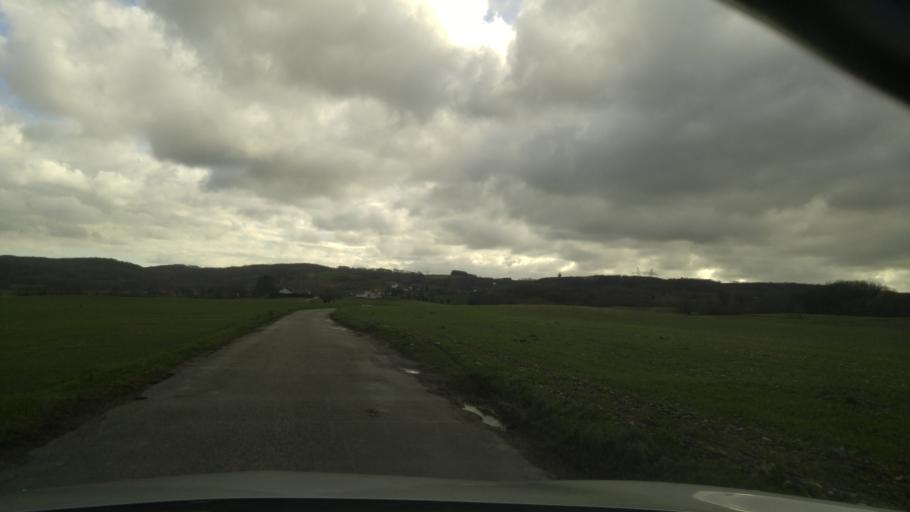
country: FR
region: Rhone-Alpes
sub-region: Departement de l'Isere
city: Roche
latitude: 45.5767
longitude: 5.1756
